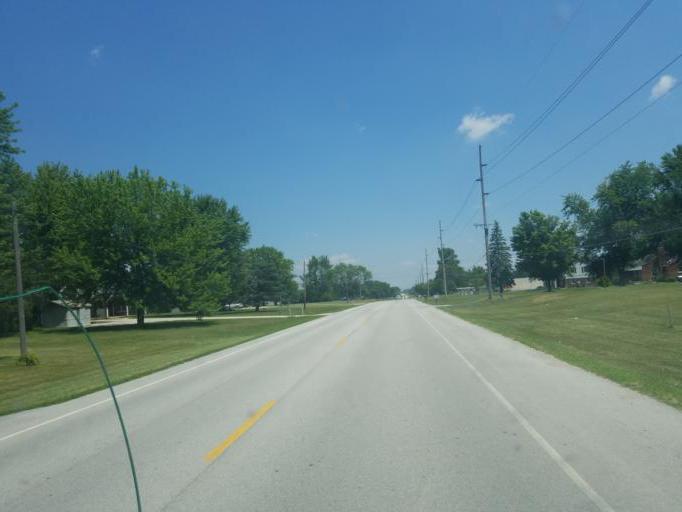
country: US
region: Ohio
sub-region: Auglaize County
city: Saint Marys
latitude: 40.5480
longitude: -84.3562
